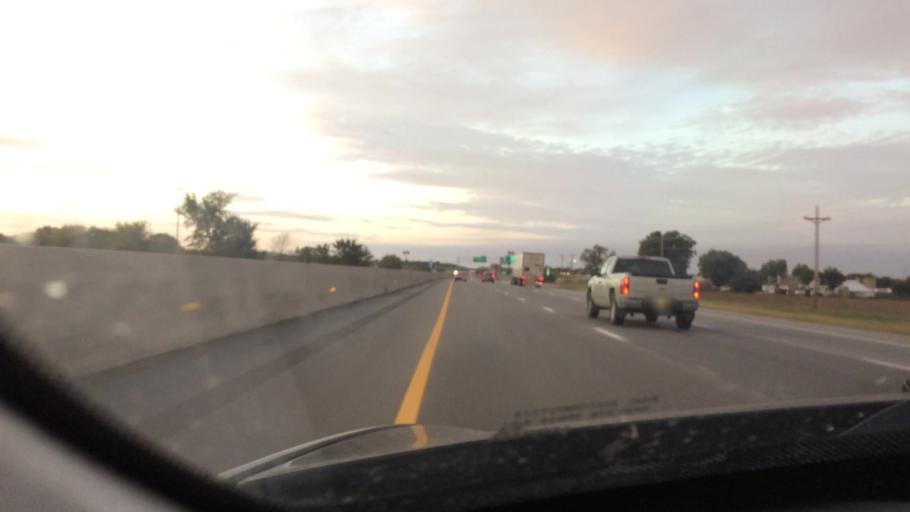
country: US
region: Ohio
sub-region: Wood County
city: North Baltimore
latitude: 41.1443
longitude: -83.6589
